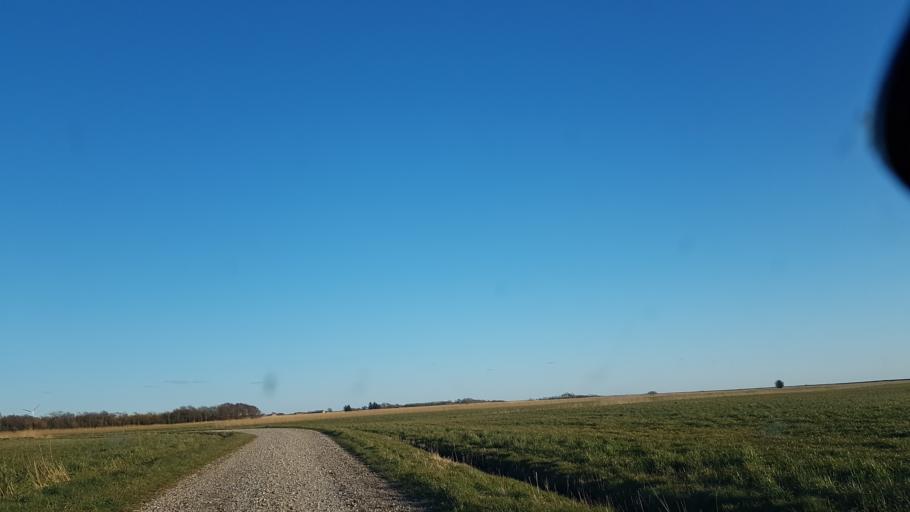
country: DK
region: South Denmark
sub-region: Esbjerg Kommune
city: Bramming
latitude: 55.4168
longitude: 8.6472
